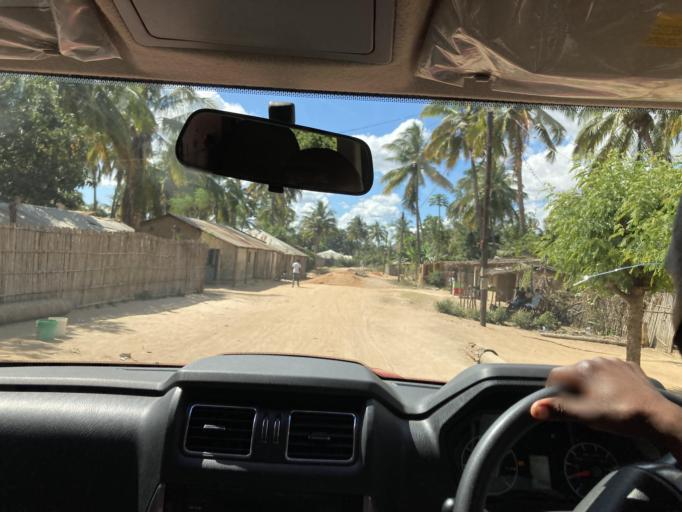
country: MZ
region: Cabo Delgado
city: Montepuez
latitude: -13.1378
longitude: 39.0013
